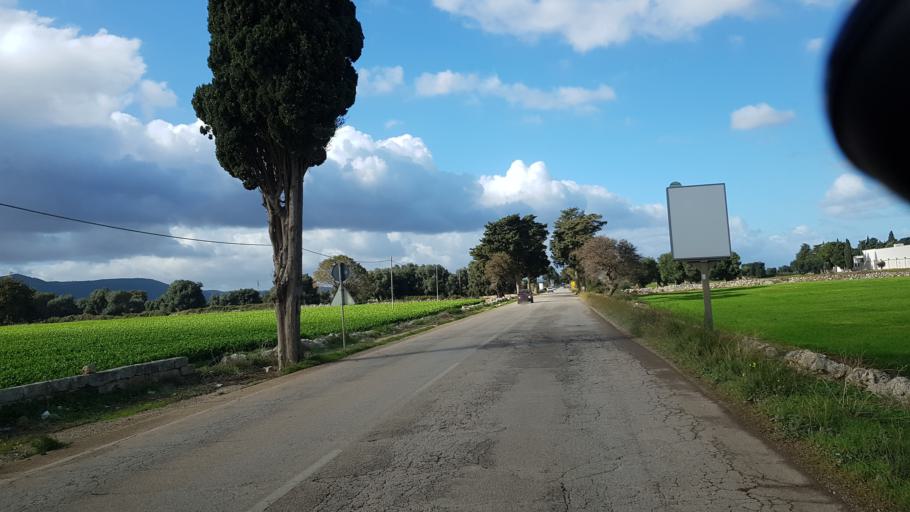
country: IT
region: Apulia
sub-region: Provincia di Brindisi
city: Montalbano
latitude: 40.7847
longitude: 17.4753
